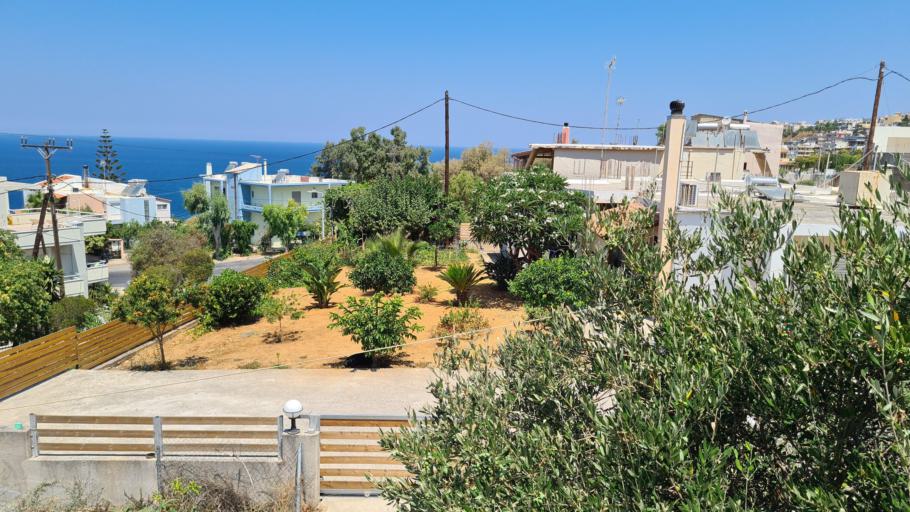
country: GR
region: Crete
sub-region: Nomos Chanias
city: Chania
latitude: 35.5214
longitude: 24.0517
